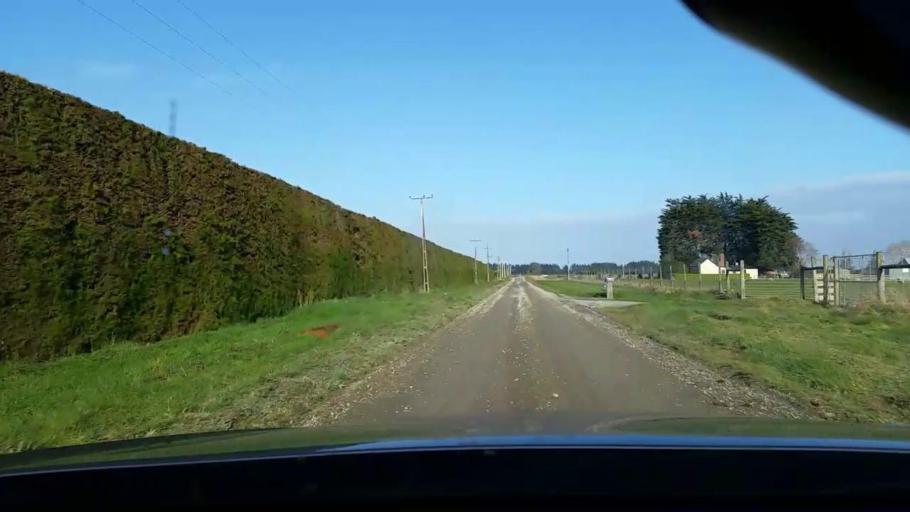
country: NZ
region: Southland
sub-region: Invercargill City
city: Invercargill
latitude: -46.2886
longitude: 168.2947
